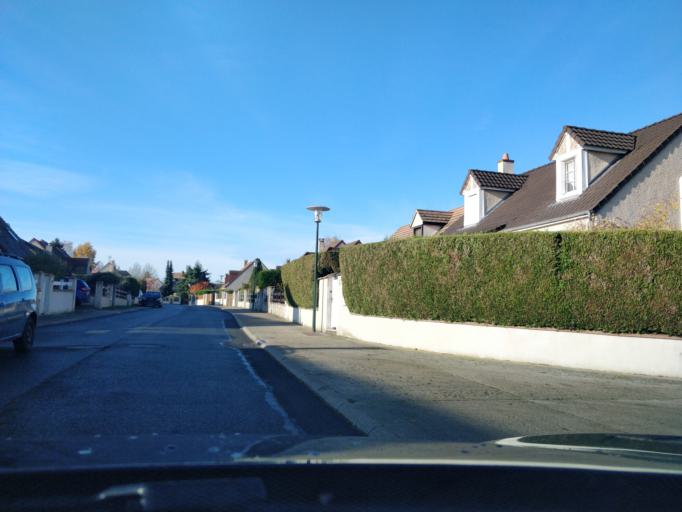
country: FR
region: Ile-de-France
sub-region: Departement de l'Essonne
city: Limours
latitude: 48.6414
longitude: 2.0686
